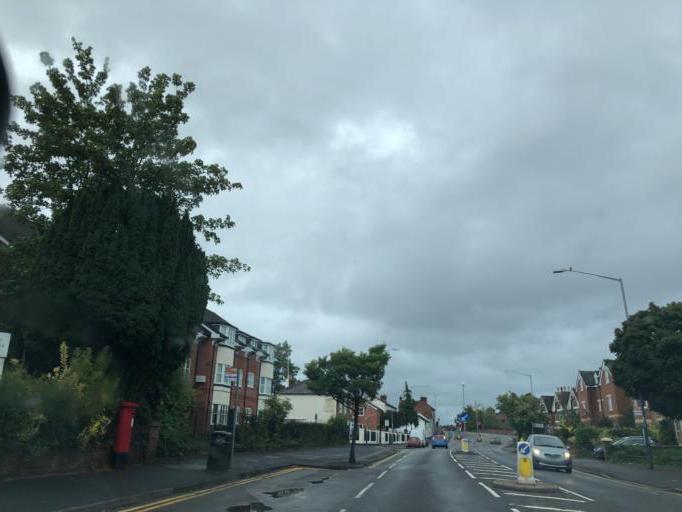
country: GB
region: England
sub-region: Warwickshire
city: Warwick
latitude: 52.2871
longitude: -1.5676
